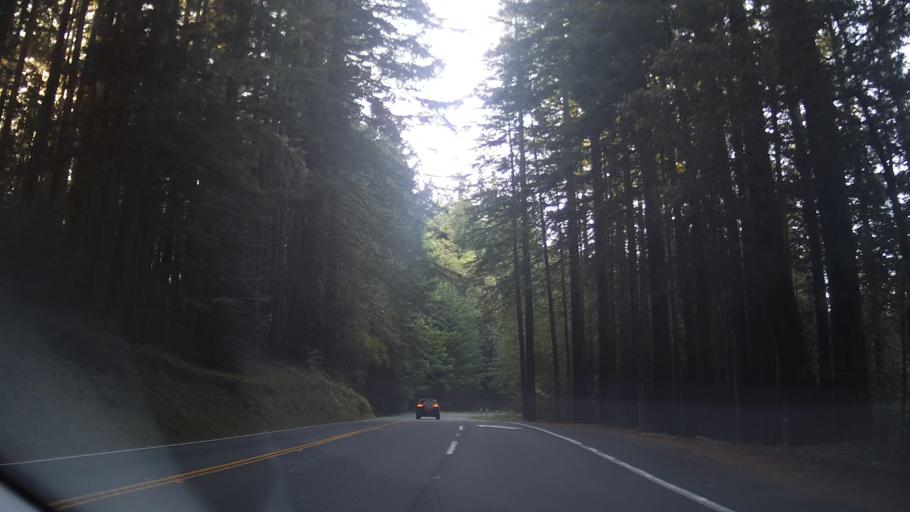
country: US
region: California
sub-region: Mendocino County
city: Fort Bragg
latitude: 39.3661
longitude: -123.6773
